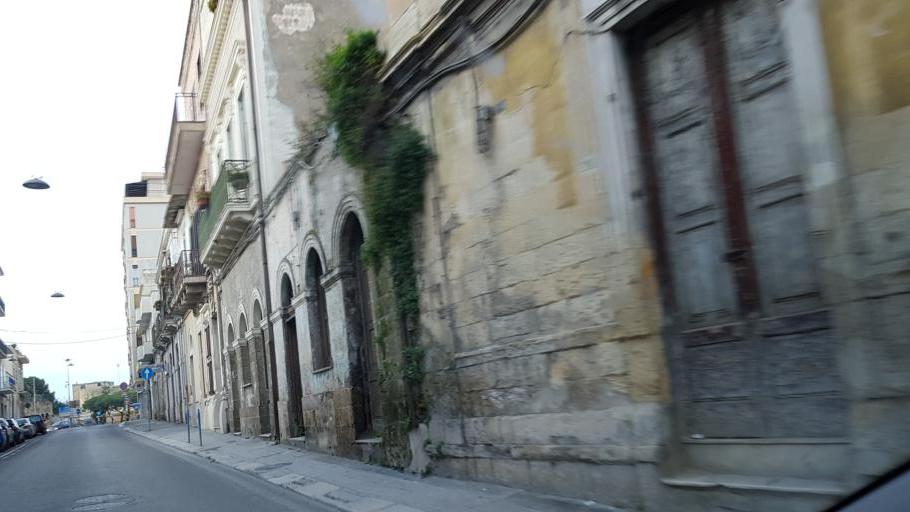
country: IT
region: Apulia
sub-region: Provincia di Brindisi
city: Brindisi
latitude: 40.6372
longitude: 17.9389
